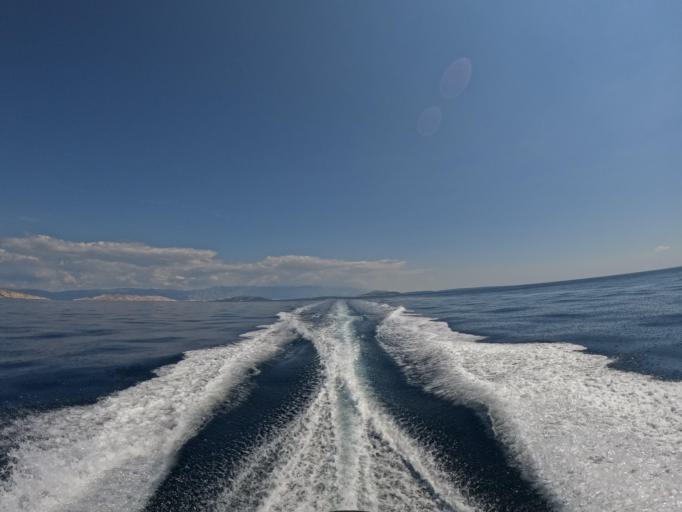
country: HR
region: Primorsko-Goranska
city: Punat
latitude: 44.9095
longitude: 14.5946
